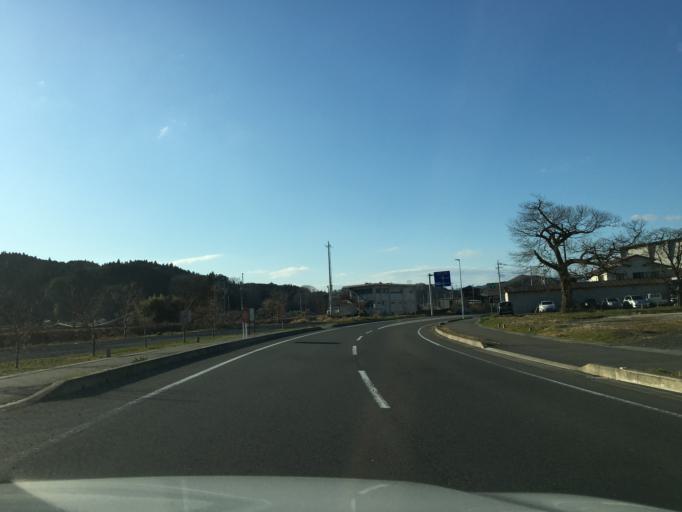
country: JP
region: Ibaraki
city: Daigo
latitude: 36.7690
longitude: 140.3528
